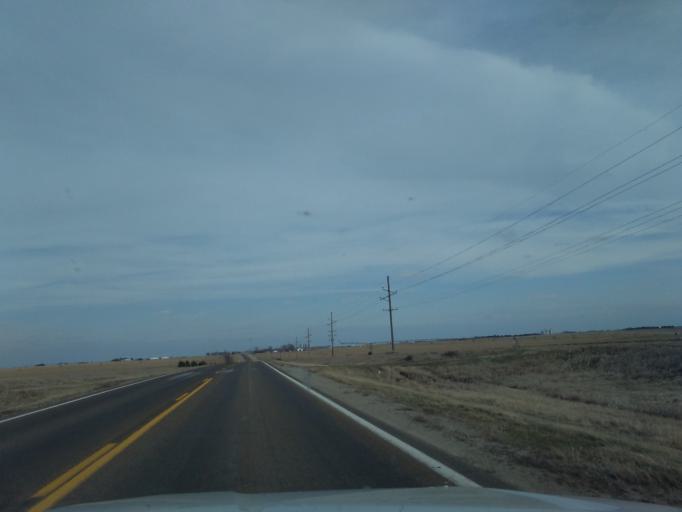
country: US
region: Nebraska
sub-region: Saline County
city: Wilber
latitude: 40.3061
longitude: -97.0547
